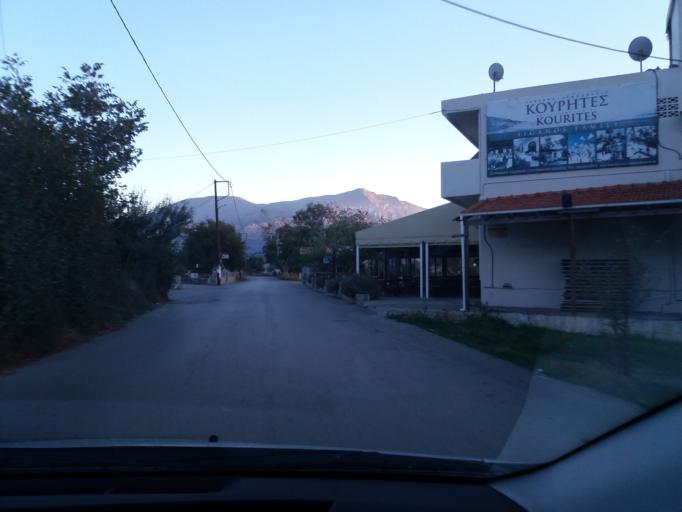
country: GR
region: Crete
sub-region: Nomos Irakleiou
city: Malia
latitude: 35.1953
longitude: 25.4894
